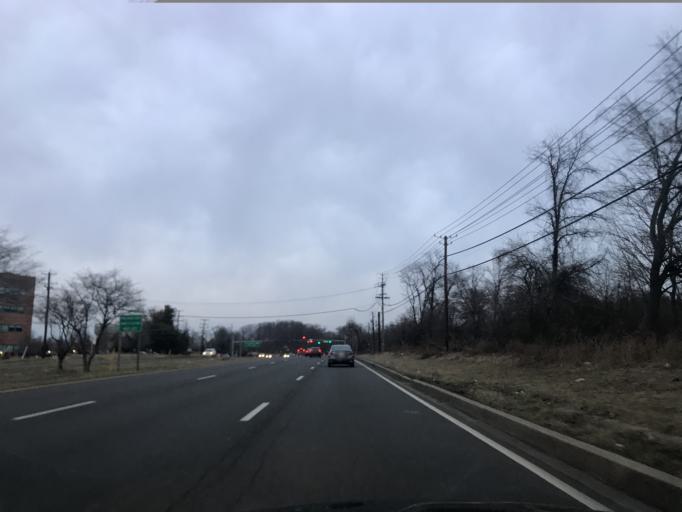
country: US
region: Maryland
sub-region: Prince George's County
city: Lake Arbor
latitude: 38.9061
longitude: -76.8341
